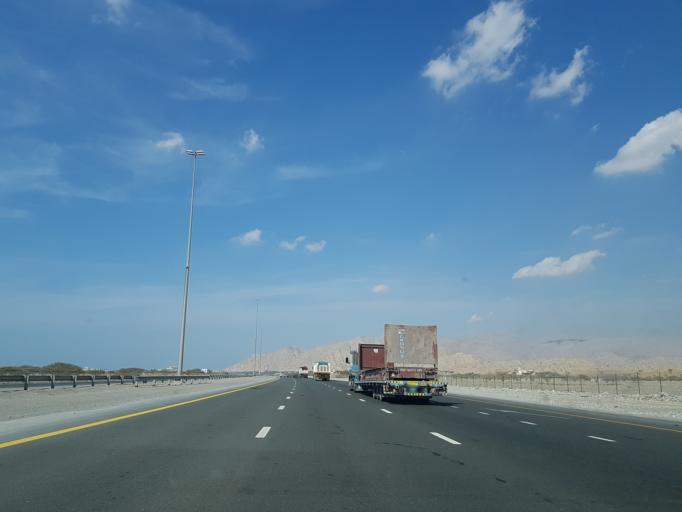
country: AE
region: Ra's al Khaymah
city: Ras al-Khaimah
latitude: 25.7848
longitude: 56.0316
